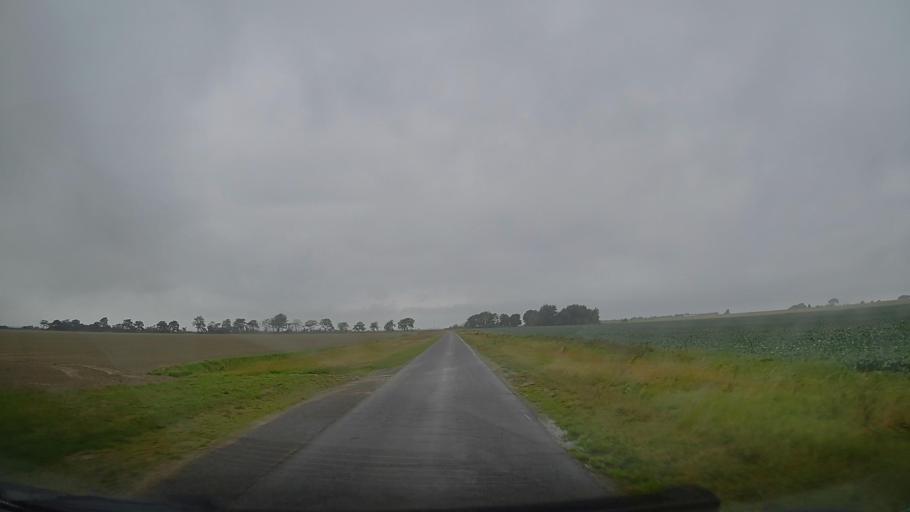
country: DE
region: Schleswig-Holstein
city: Epenwohrden
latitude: 54.1015
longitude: 8.9925
